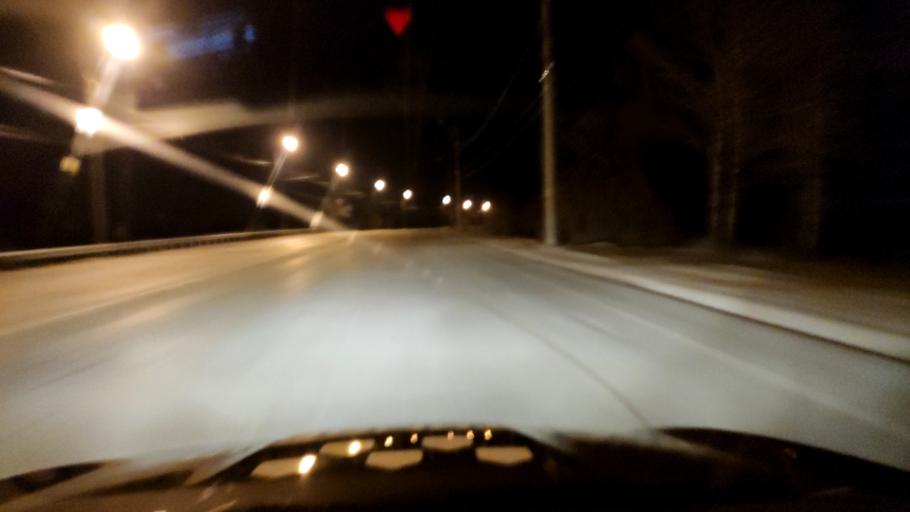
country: RU
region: Samara
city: Zhigulevsk
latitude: 53.5086
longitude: 49.5199
